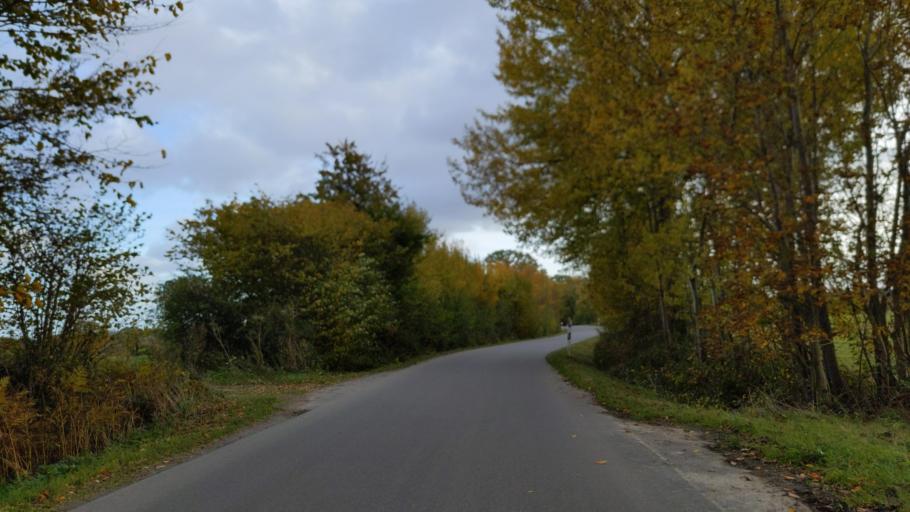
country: DE
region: Schleswig-Holstein
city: Kasseedorf
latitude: 54.1251
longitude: 10.7078
